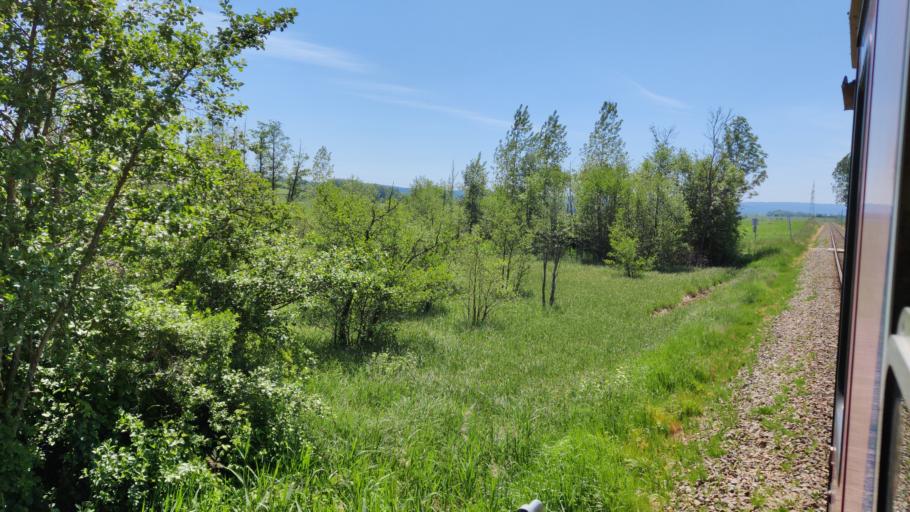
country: AT
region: Lower Austria
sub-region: Politischer Bezirk Horn
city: Horn
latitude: 48.6527
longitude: 15.6751
